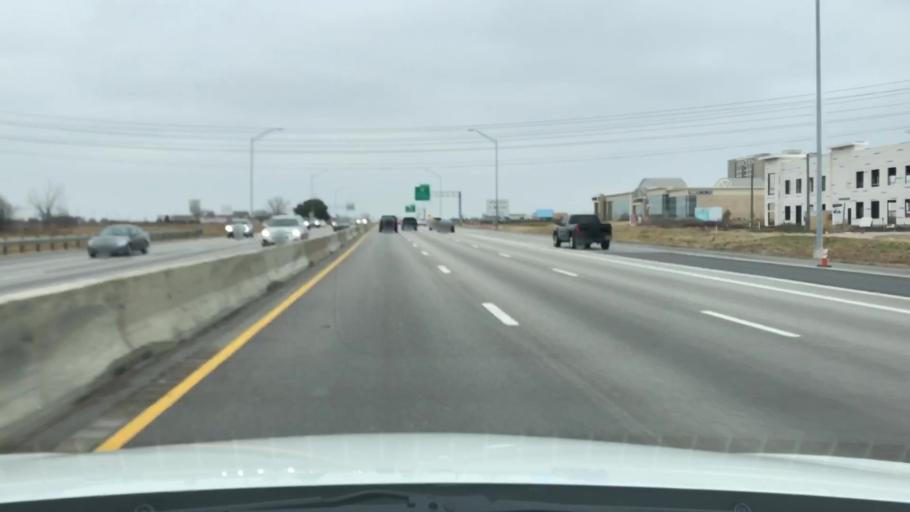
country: US
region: Texas
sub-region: Denton County
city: Denton
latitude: 33.2186
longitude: -97.1702
